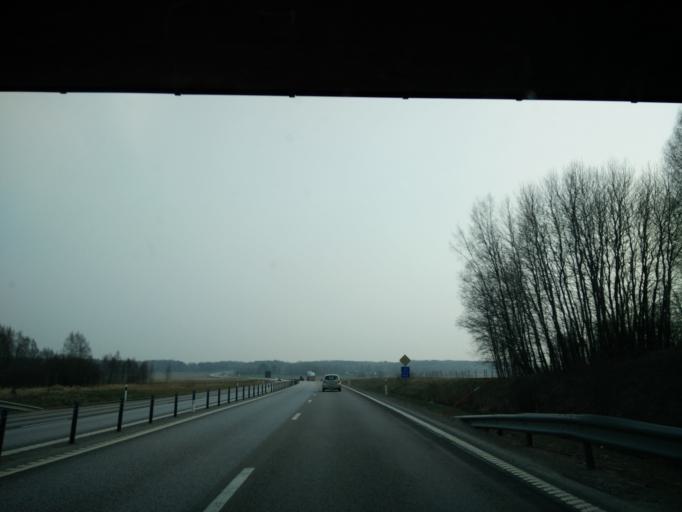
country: SE
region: Vaermland
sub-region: Karlstads Kommun
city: Karlstad
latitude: 59.4228
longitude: 13.4092
